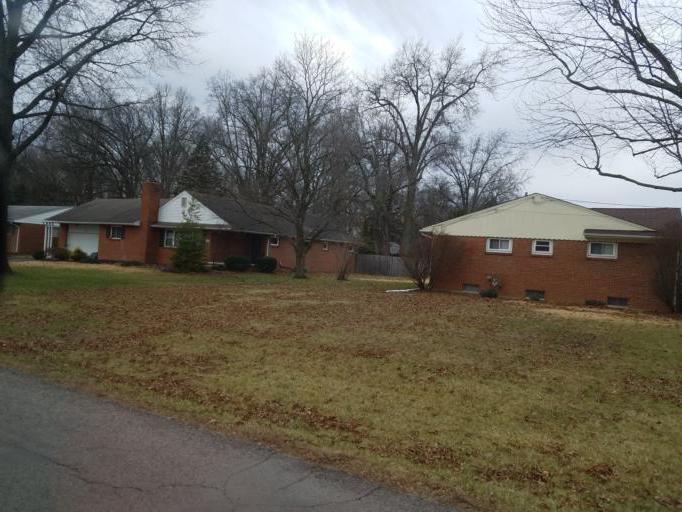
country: US
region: Ohio
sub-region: Marion County
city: Marion
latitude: 40.5790
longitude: -83.0972
